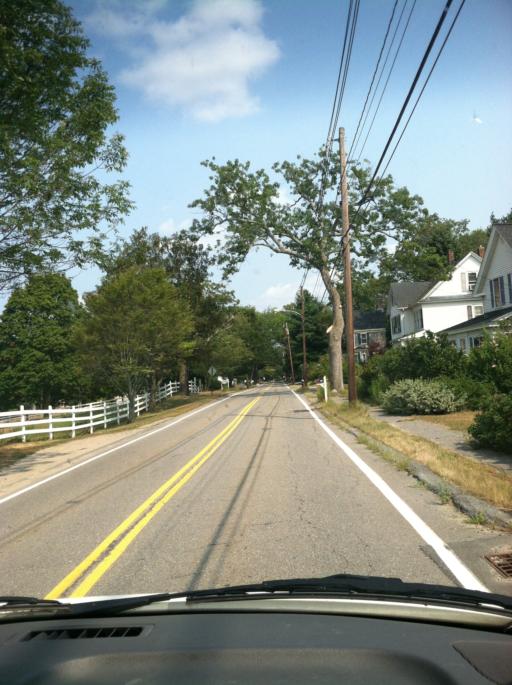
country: US
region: Massachusetts
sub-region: Middlesex County
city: West Concord
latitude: 42.4680
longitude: -71.3930
